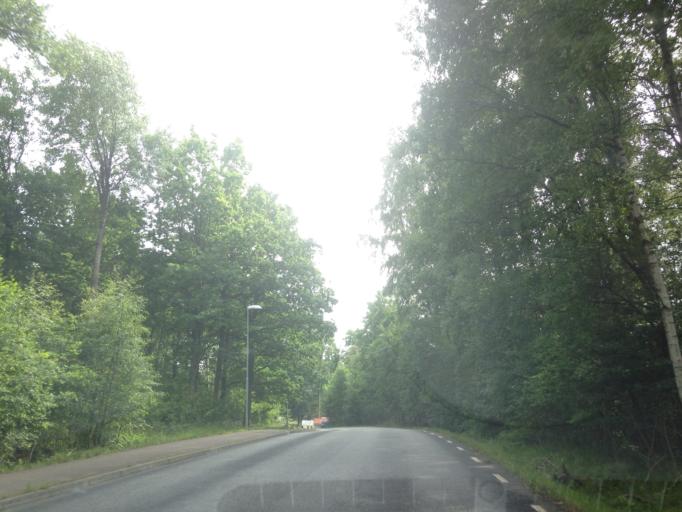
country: SE
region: Vaestra Goetaland
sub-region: Goteborg
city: Goeteborg
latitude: 57.7741
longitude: 11.9523
